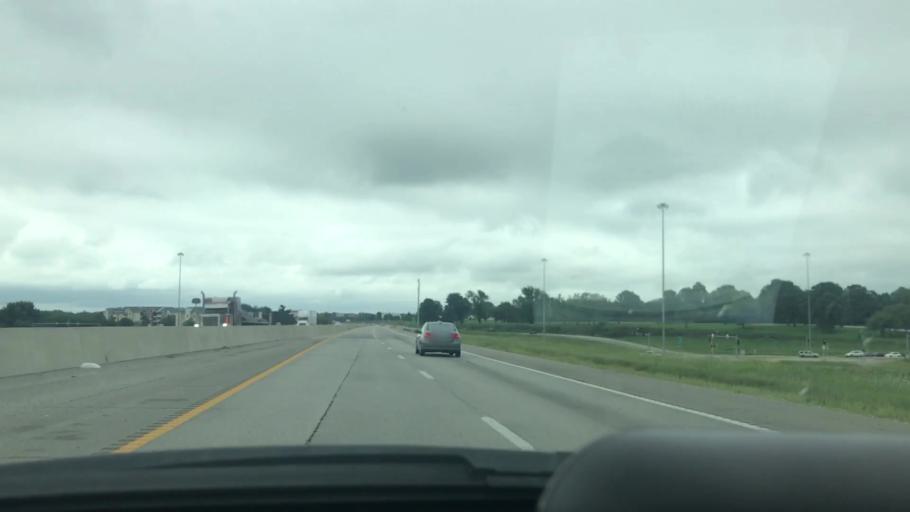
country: US
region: Missouri
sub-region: Jasper County
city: Duquesne
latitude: 37.0463
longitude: -94.4812
